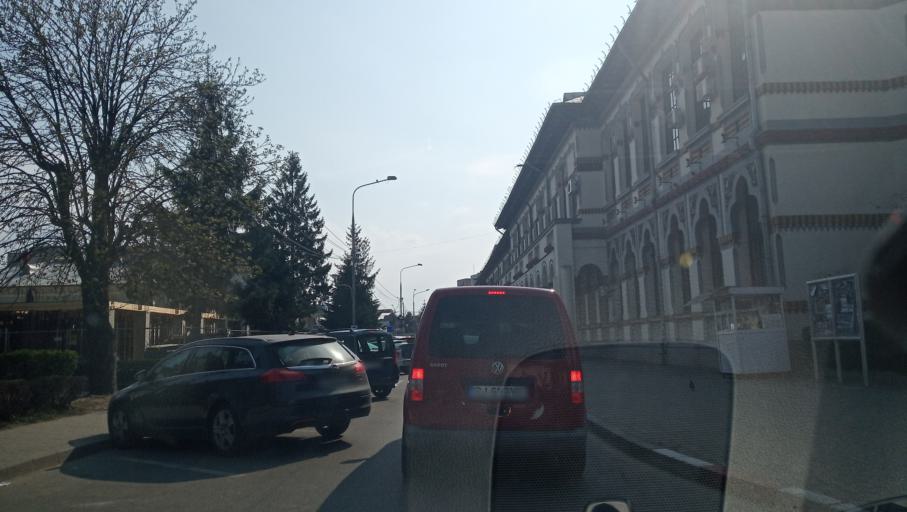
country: RO
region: Gorj
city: Targu Jiu
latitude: 45.0385
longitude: 23.2752
